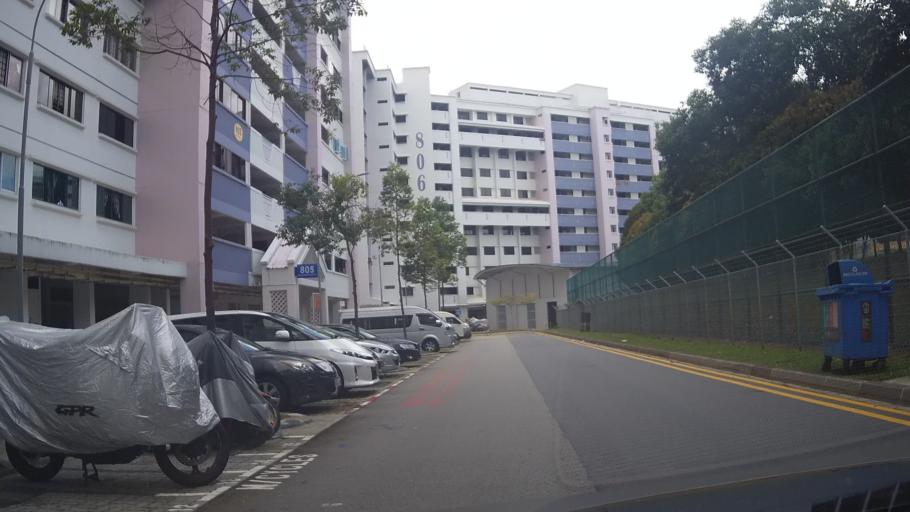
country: MY
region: Johor
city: Johor Bahru
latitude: 1.4407
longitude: 103.7878
